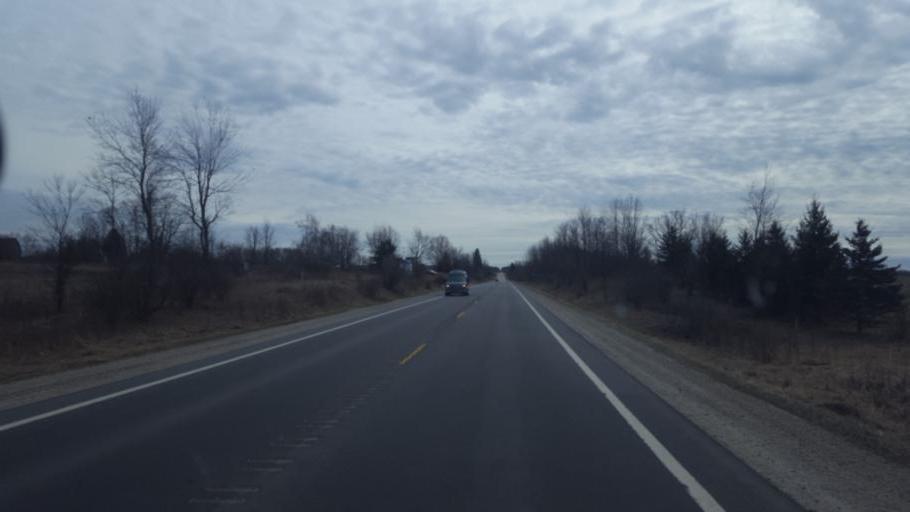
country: US
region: Michigan
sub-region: Isabella County
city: Lake Isabella
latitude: 43.7148
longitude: -85.1467
